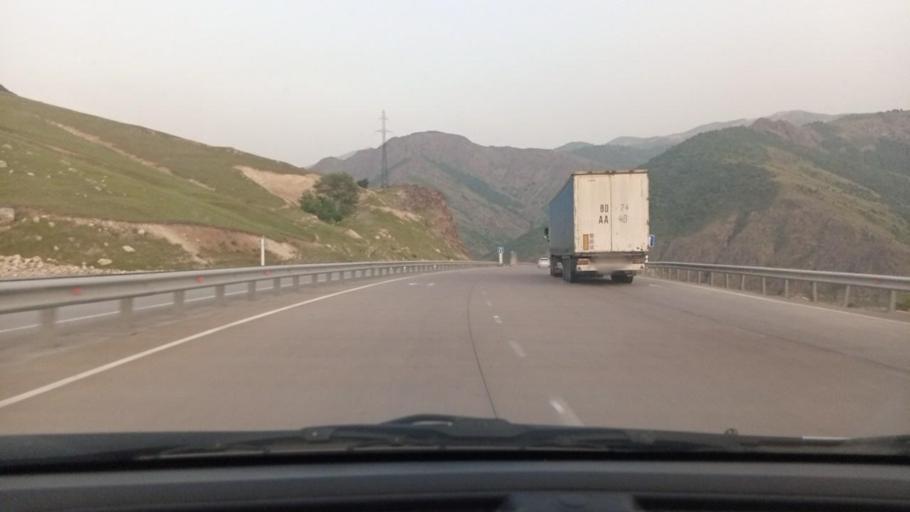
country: UZ
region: Toshkent
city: Angren
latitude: 41.0741
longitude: 70.2673
